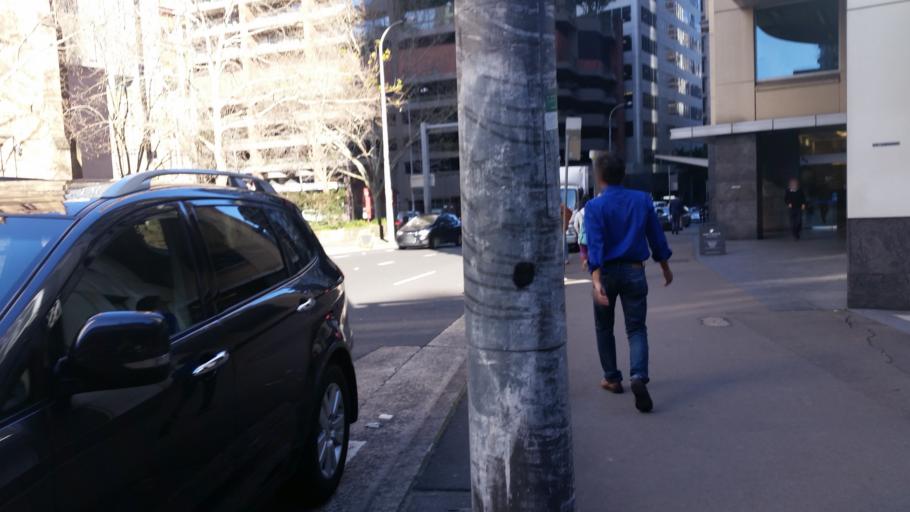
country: AU
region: New South Wales
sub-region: City of Sydney
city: Sydney
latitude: -33.8639
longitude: 151.2045
